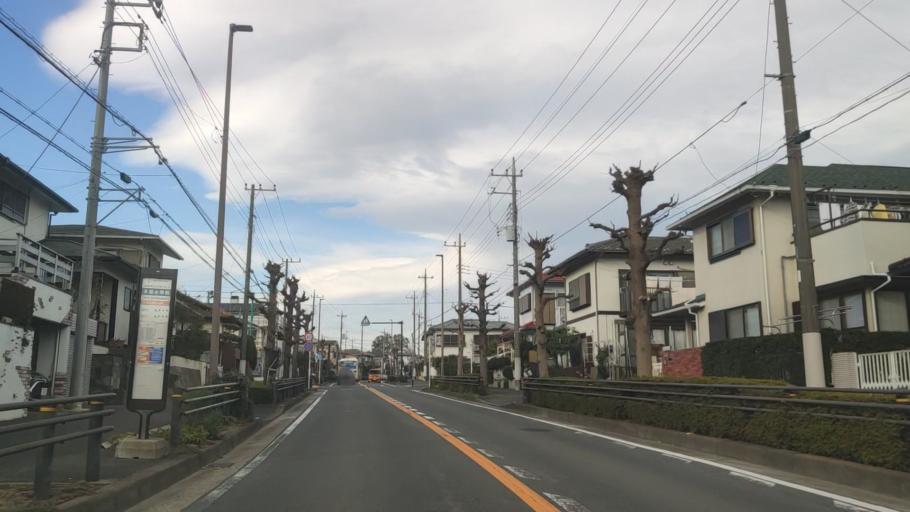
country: JP
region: Kanagawa
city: Atsugi
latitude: 35.4420
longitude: 139.4026
